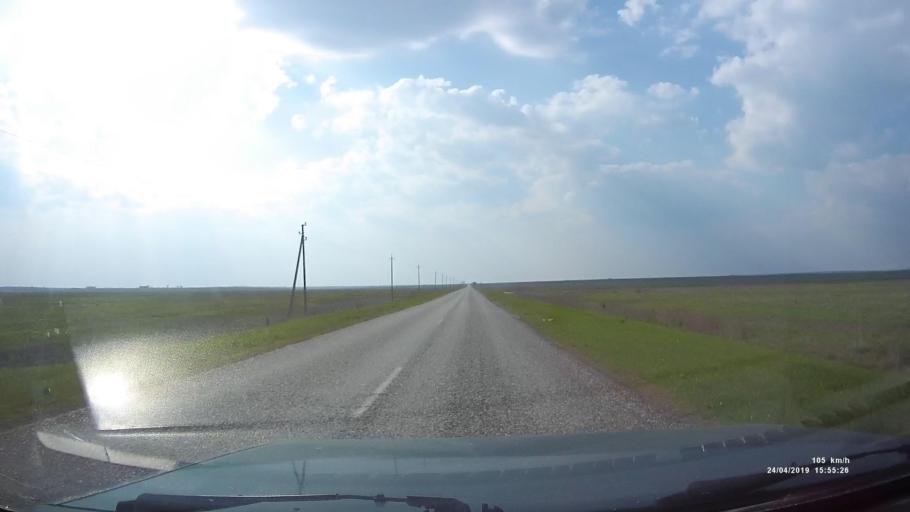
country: RU
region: Kalmykiya
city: Yashalta
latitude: 46.5905
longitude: 42.5493
